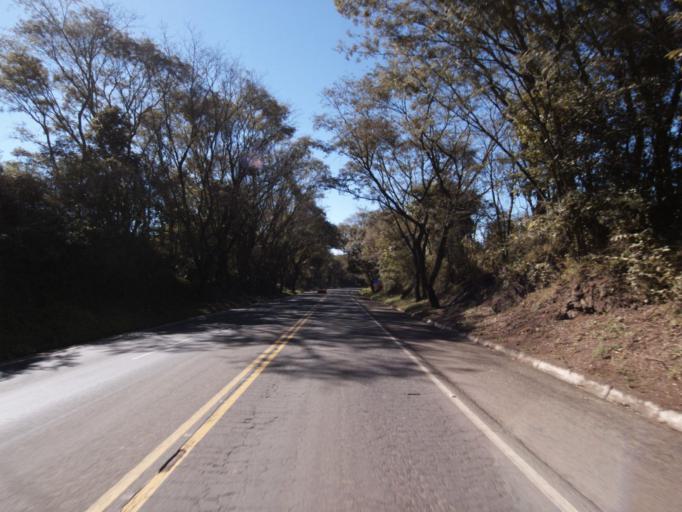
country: BR
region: Santa Catarina
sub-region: Sao Lourenco Do Oeste
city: Sao Lourenco dOeste
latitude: -26.8262
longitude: -53.0736
